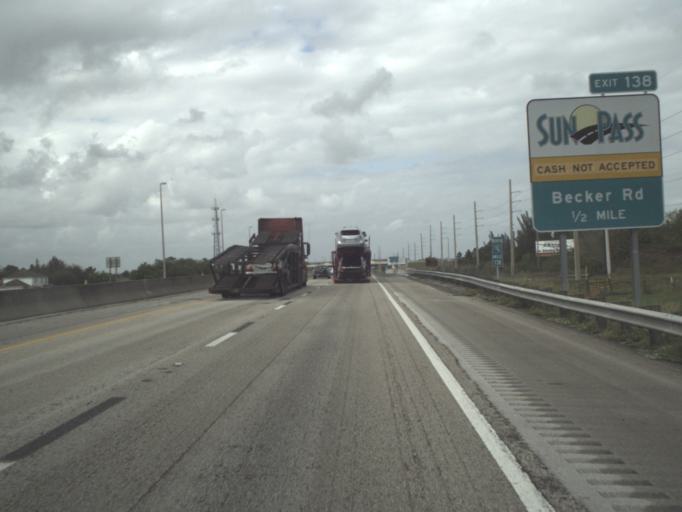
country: US
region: Florida
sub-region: Martin County
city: North River Shores
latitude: 27.2043
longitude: -80.3311
